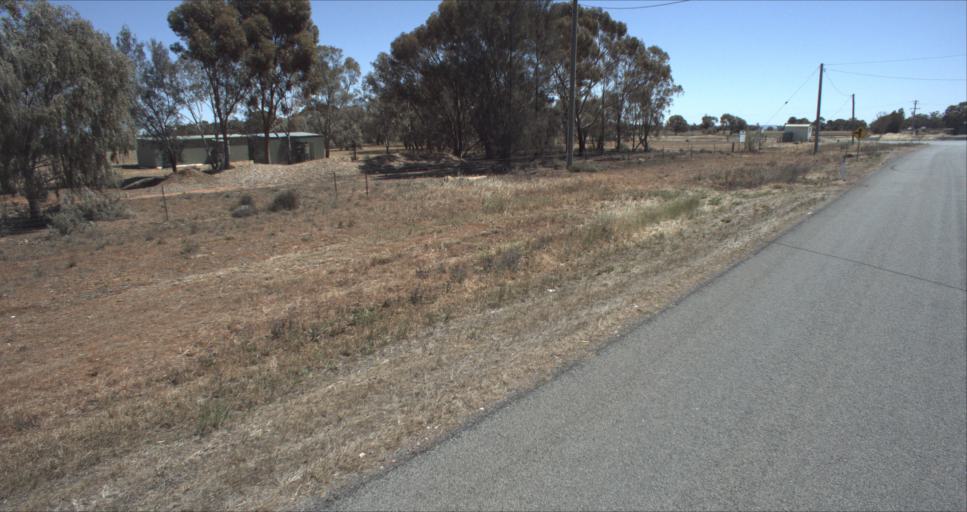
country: AU
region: New South Wales
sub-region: Leeton
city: Leeton
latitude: -34.4284
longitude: 146.3001
